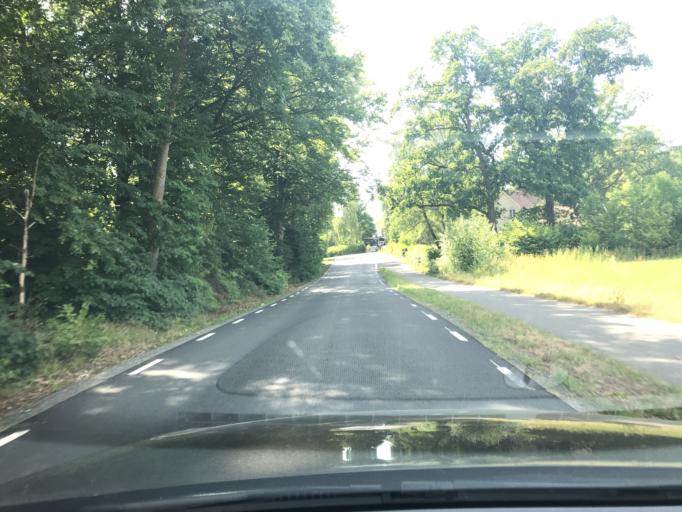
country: SE
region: Skane
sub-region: Hassleholms Kommun
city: Hastveda
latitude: 56.2729
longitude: 13.9022
